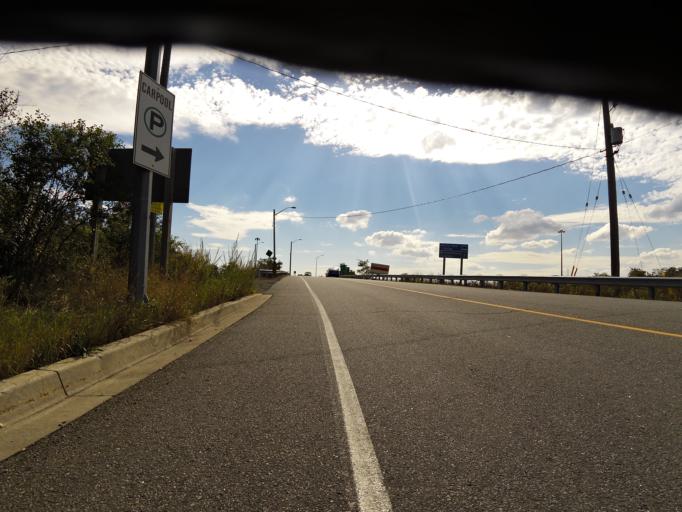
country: CA
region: Ontario
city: Hamilton
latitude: 43.3037
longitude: -79.9037
